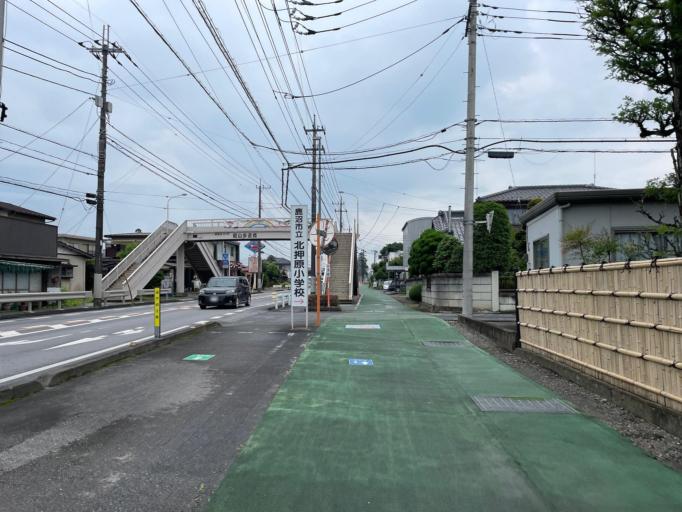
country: JP
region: Tochigi
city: Kanuma
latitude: 36.5337
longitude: 139.7476
